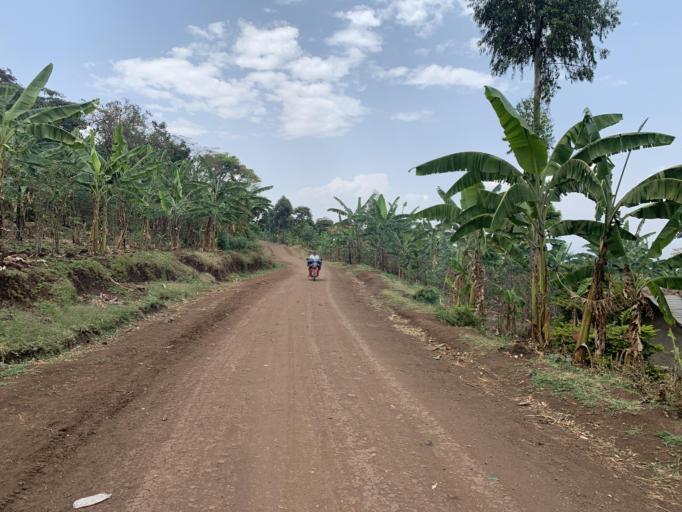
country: UG
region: Eastern Region
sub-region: Sironko District
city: Sironko
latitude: 1.2575
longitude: 34.3100
